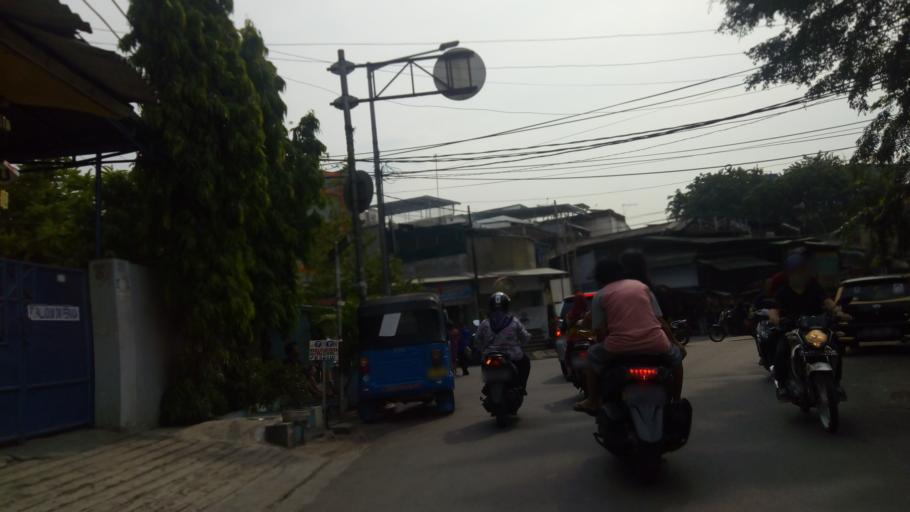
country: ID
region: Jakarta Raya
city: Jakarta
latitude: -6.1689
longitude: 106.8497
